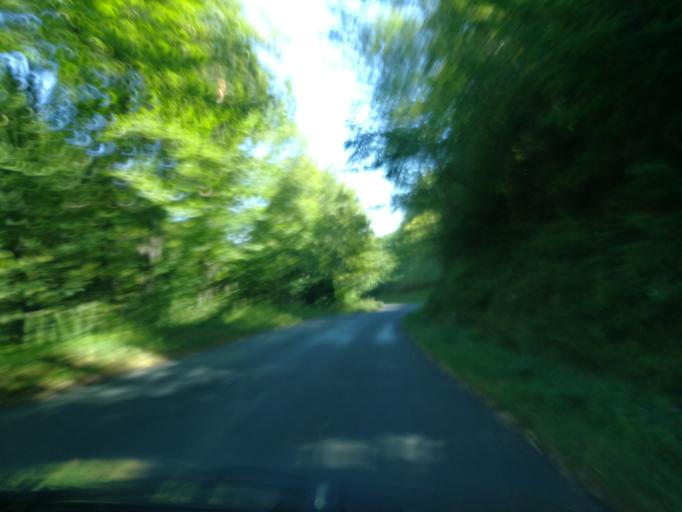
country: FR
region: Limousin
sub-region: Departement de la Correze
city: Argentat
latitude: 45.0923
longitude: 1.9145
